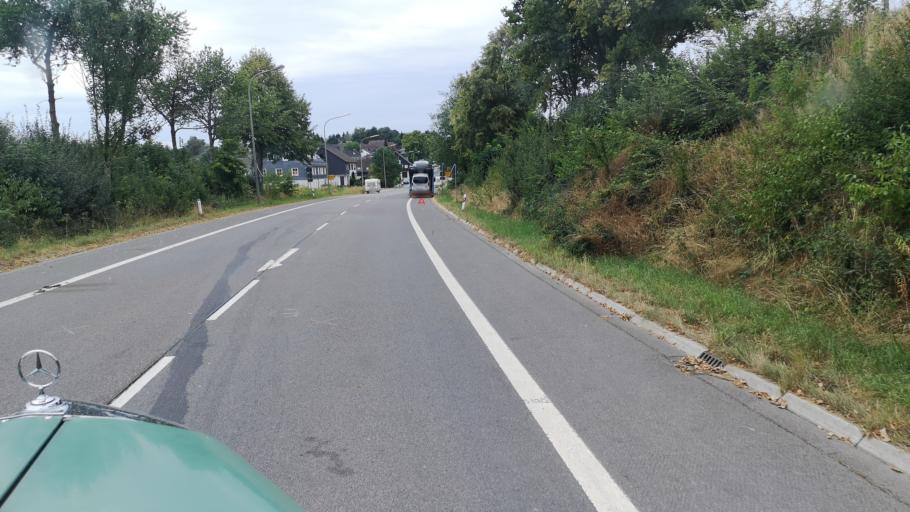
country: DE
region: North Rhine-Westphalia
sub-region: Regierungsbezirk Koln
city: Kurten
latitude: 51.0660
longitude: 7.2422
